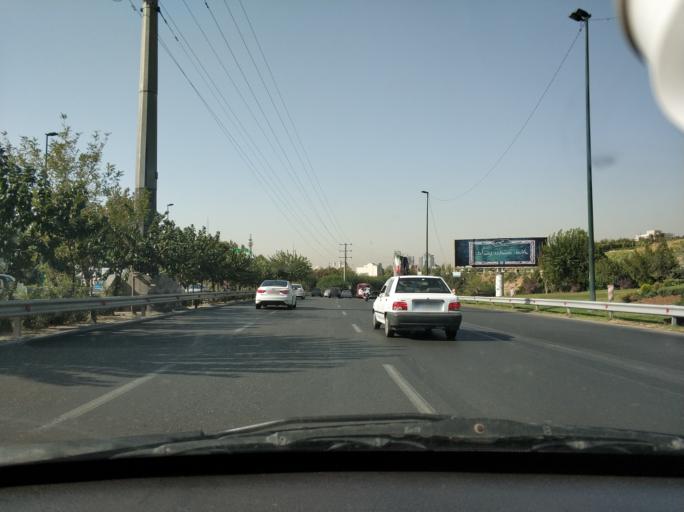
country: IR
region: Tehran
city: Tehran
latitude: 35.7417
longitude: 51.4335
